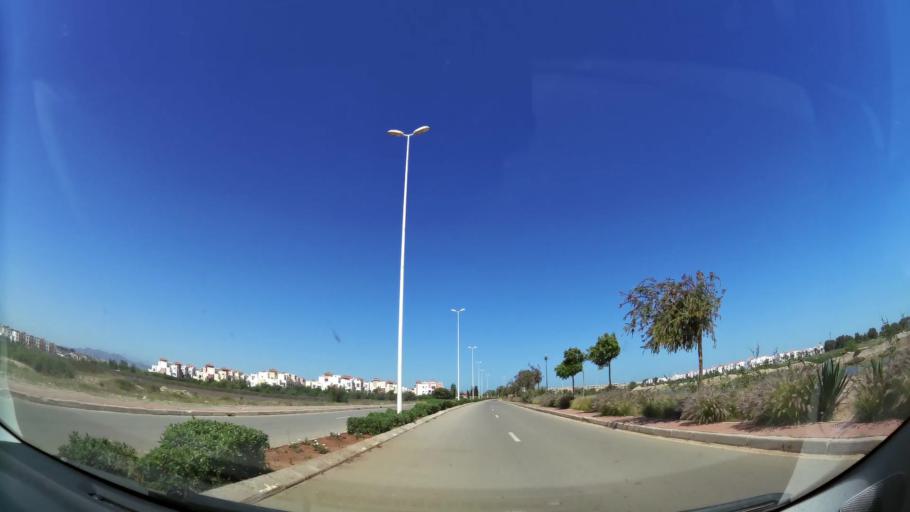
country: MA
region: Oriental
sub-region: Berkane-Taourirt
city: Madagh
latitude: 35.1038
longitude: -2.3080
